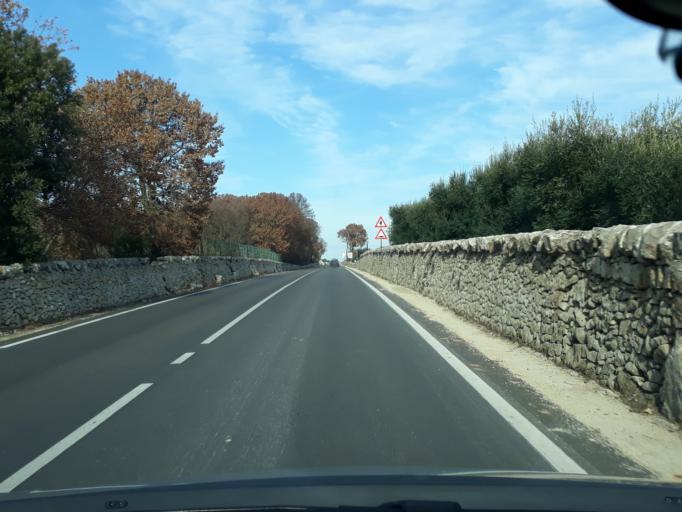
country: IT
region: Apulia
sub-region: Provincia di Bari
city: Locorotondo
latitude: 40.7708
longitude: 17.3341
